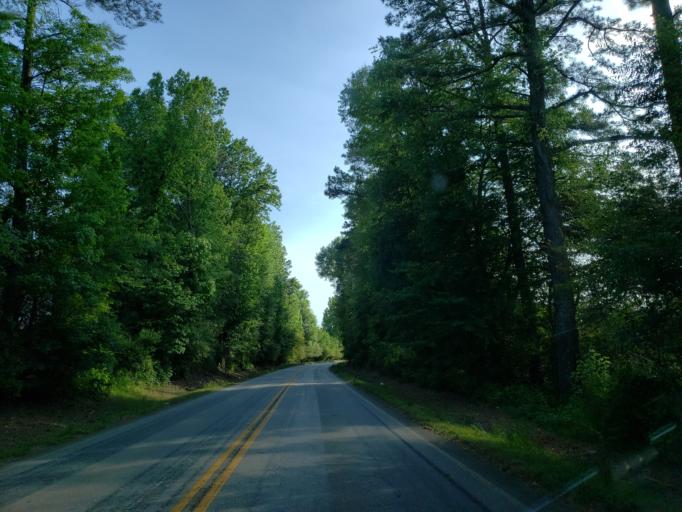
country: US
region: Georgia
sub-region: Carroll County
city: Bowdon
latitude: 33.4681
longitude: -85.2976
